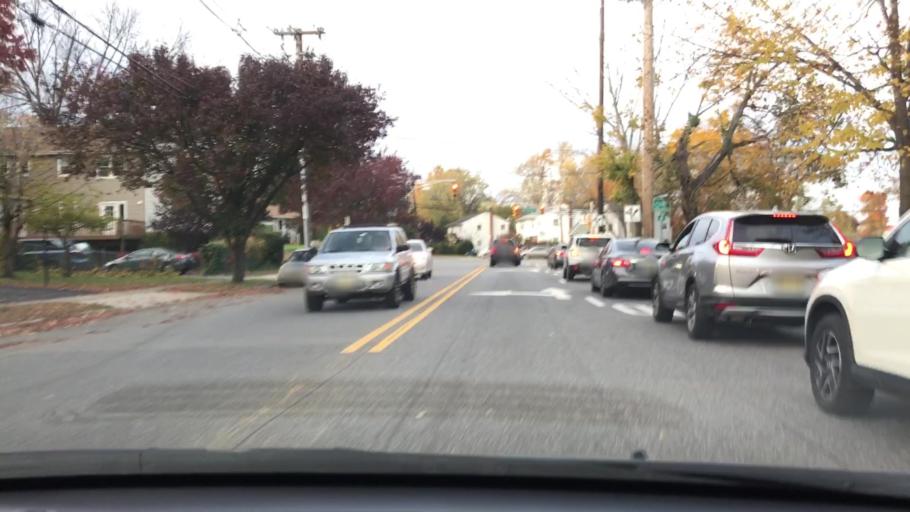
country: US
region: New Jersey
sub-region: Bergen County
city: Bergenfield
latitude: 40.9133
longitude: -74.0024
